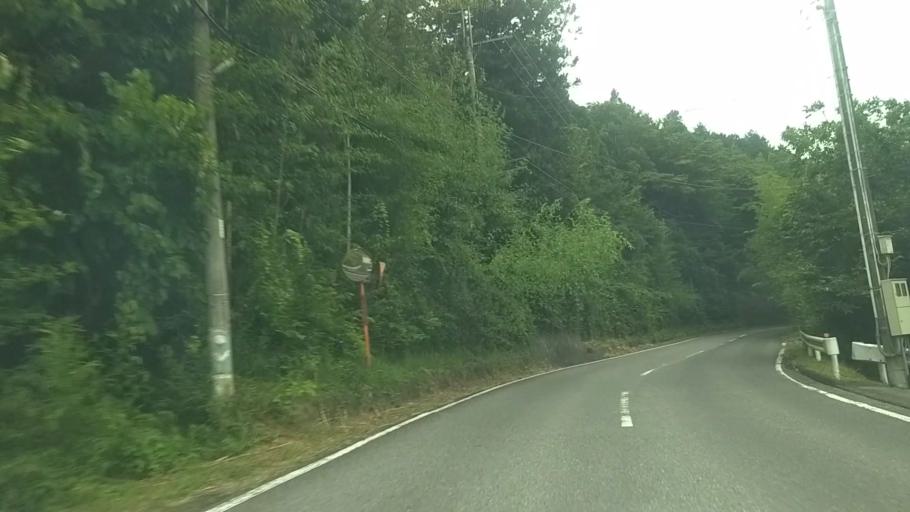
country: JP
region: Chiba
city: Kimitsu
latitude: 35.2321
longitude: 140.0093
